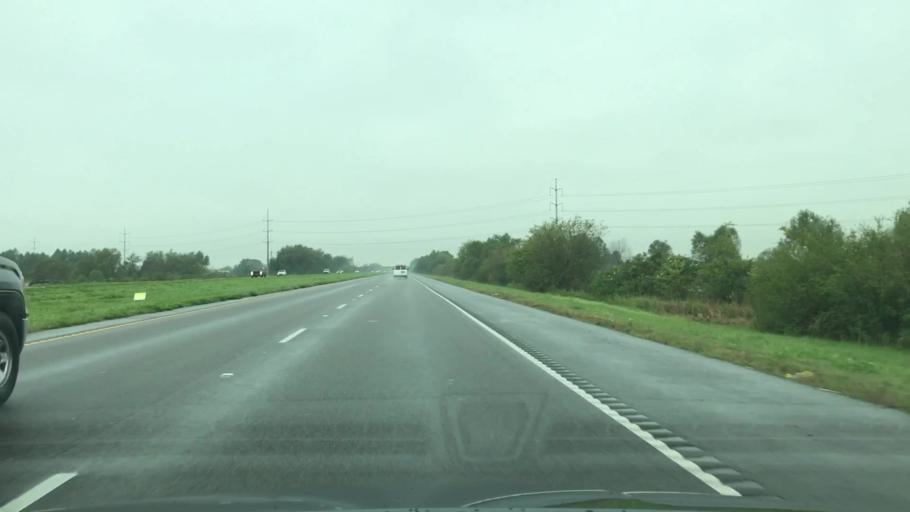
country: US
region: Louisiana
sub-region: Lafourche Parish
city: Raceland
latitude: 29.6901
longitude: -90.6094
